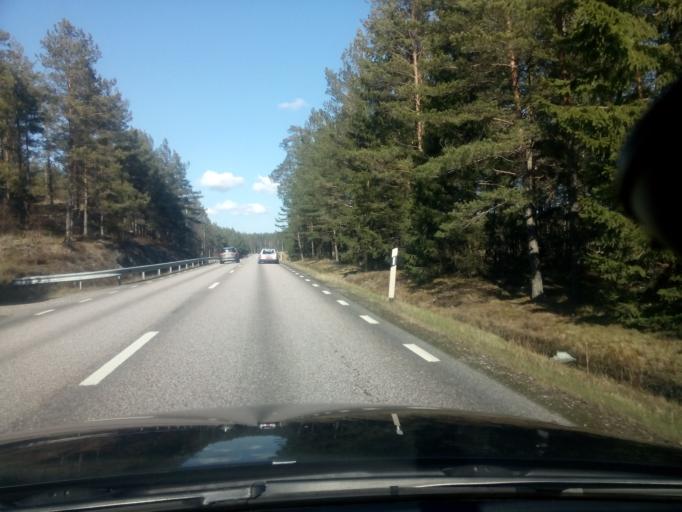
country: SE
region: Soedermanland
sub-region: Strangnas Kommun
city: Akers Styckebruk
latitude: 59.2223
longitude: 16.9134
